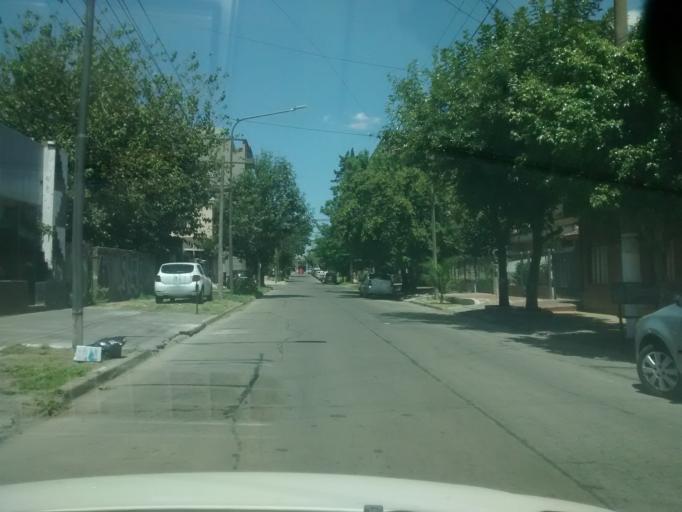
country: AR
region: Buenos Aires
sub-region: Partido de Moron
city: Moron
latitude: -34.6577
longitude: -58.6164
